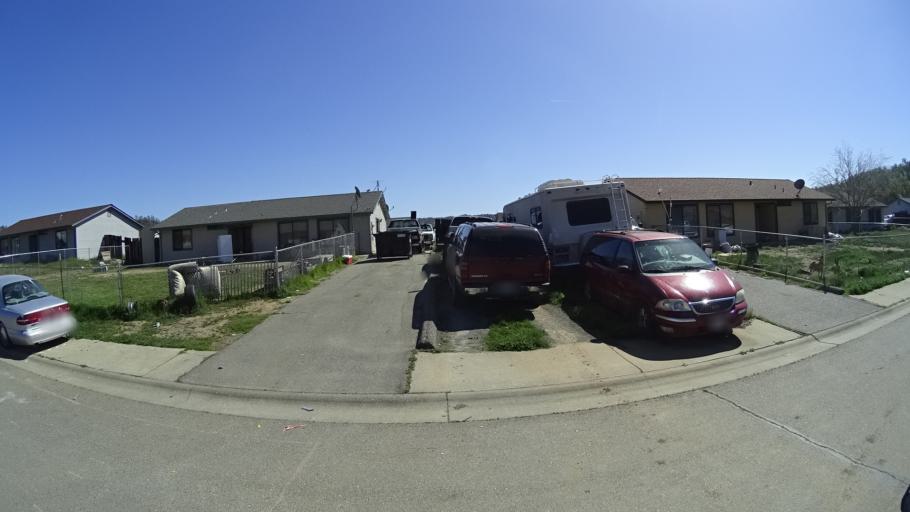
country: US
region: California
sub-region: Glenn County
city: Orland
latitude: 39.6750
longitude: -122.5216
